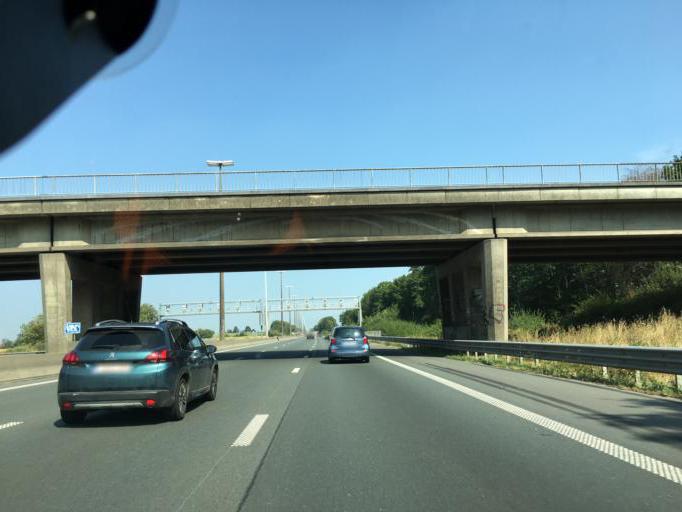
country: BE
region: Wallonia
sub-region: Province du Hainaut
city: Fleurus
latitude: 50.4738
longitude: 4.5563
